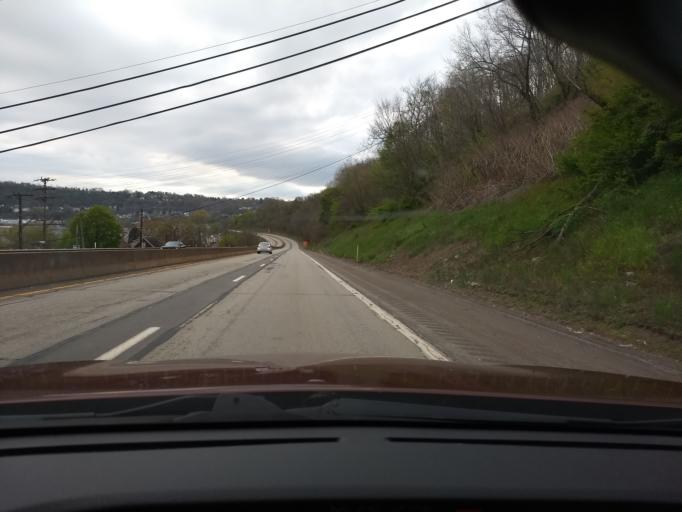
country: US
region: Pennsylvania
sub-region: Allegheny County
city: Wilmerding
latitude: 40.4005
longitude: -79.8144
